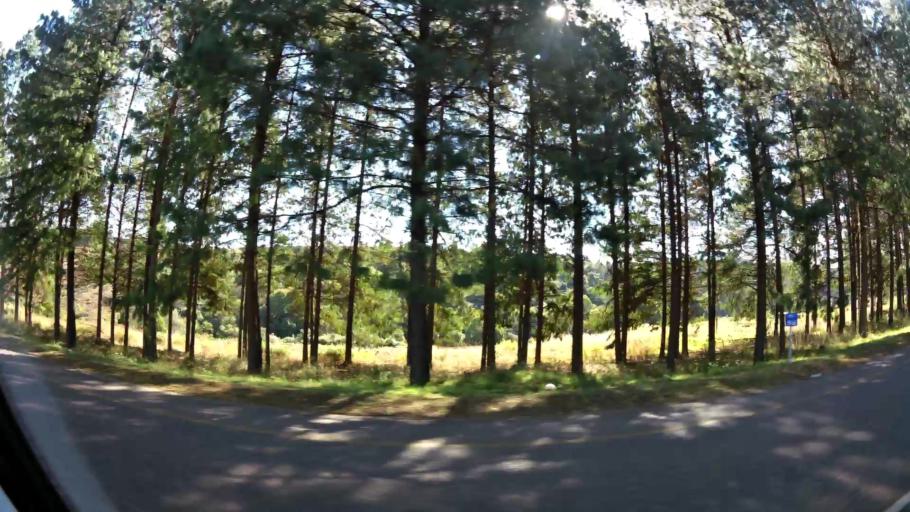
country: ZA
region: Limpopo
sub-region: Capricorn District Municipality
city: Mankoeng
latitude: -23.9345
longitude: 29.9549
